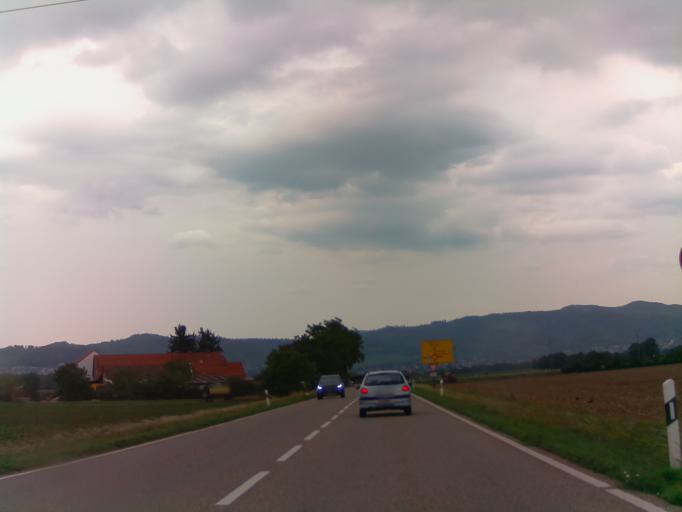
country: DE
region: Baden-Wuerttemberg
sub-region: Karlsruhe Region
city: Heddesheim
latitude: 49.5342
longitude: 8.6152
